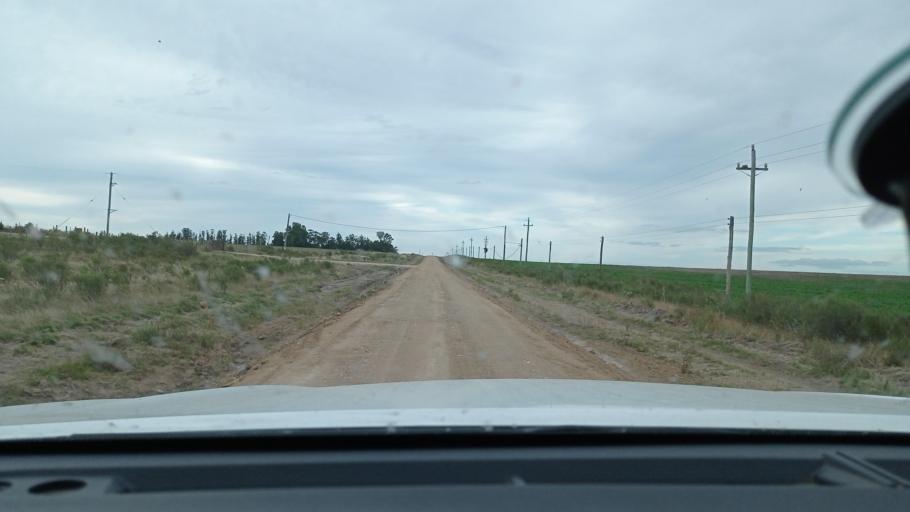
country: UY
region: Florida
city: Casupa
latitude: -34.1160
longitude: -55.7683
